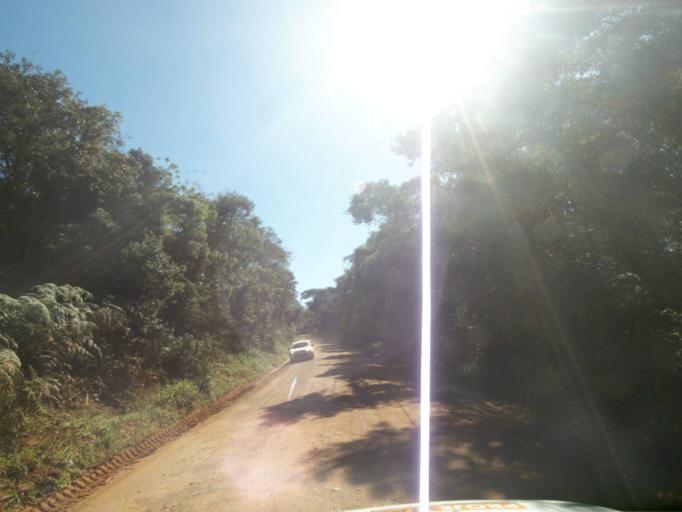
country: BR
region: Parana
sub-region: Tibagi
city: Tibagi
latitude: -24.5787
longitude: -50.6191
